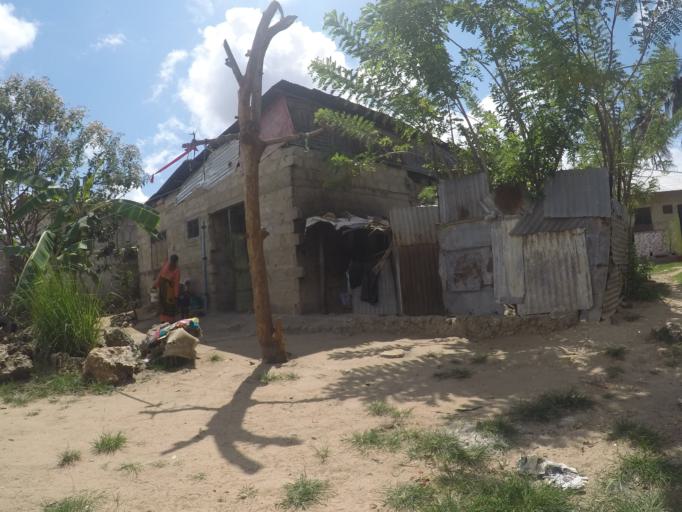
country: TZ
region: Zanzibar Urban/West
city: Zanzibar
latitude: -6.2010
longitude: 39.2387
